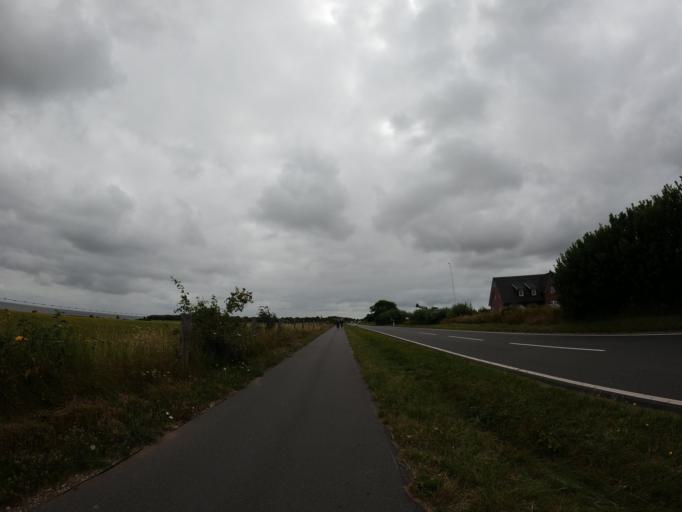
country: DE
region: Schleswig-Holstein
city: Tinnum
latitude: 54.9445
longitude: 8.3476
